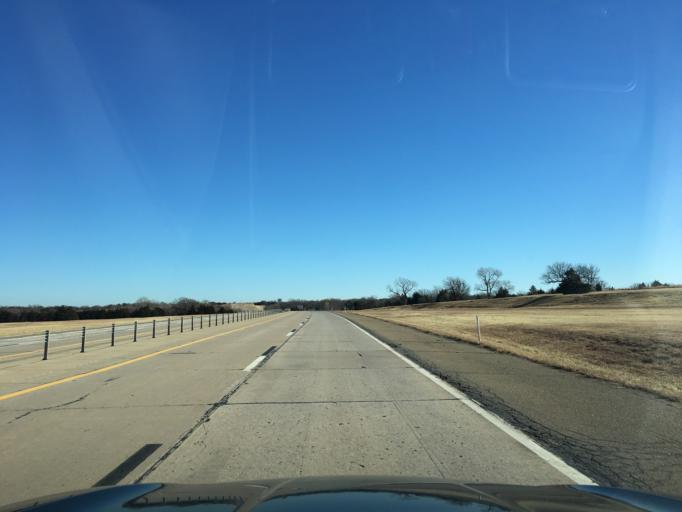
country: US
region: Oklahoma
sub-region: Payne County
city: Stillwater
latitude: 36.2412
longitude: -96.9492
